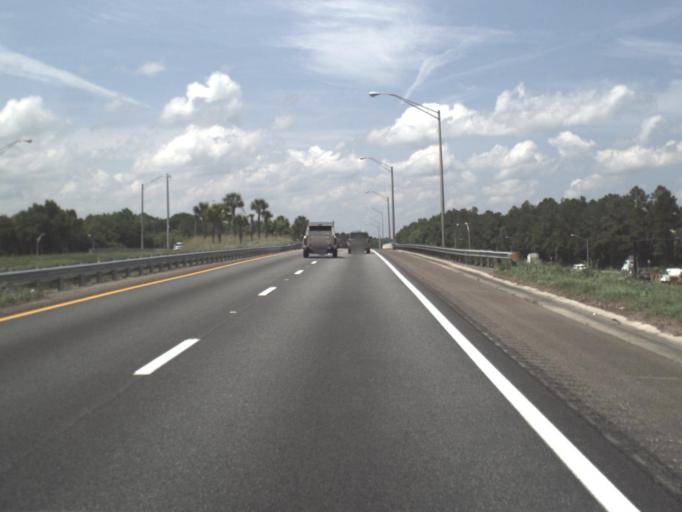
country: US
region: Florida
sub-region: Duval County
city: Jacksonville
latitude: 30.3706
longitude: -81.7609
